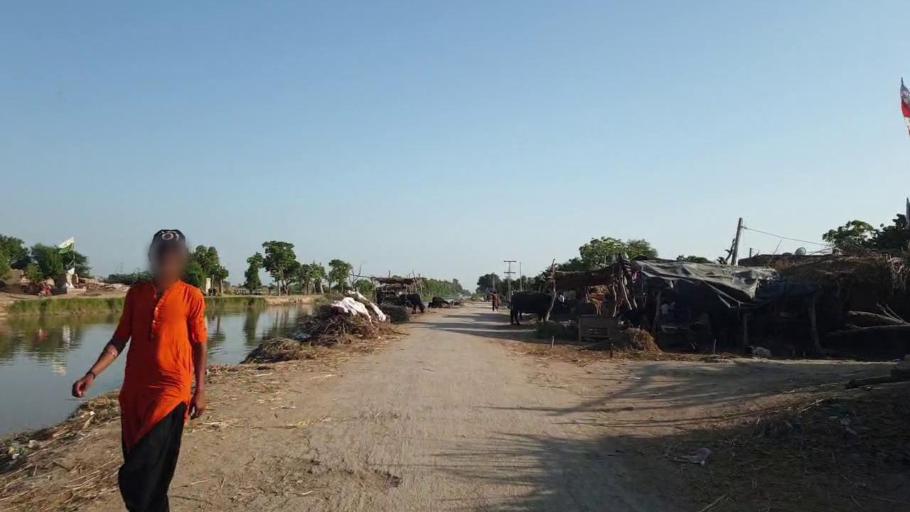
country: PK
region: Sindh
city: Hyderabad
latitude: 25.3234
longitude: 68.4267
